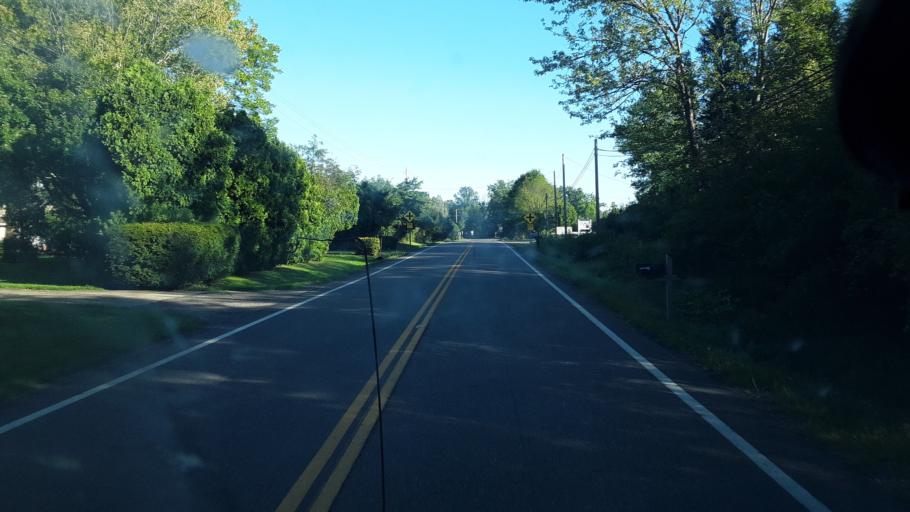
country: US
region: Ohio
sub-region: Trumbull County
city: Leavittsburg
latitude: 41.3370
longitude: -80.9568
